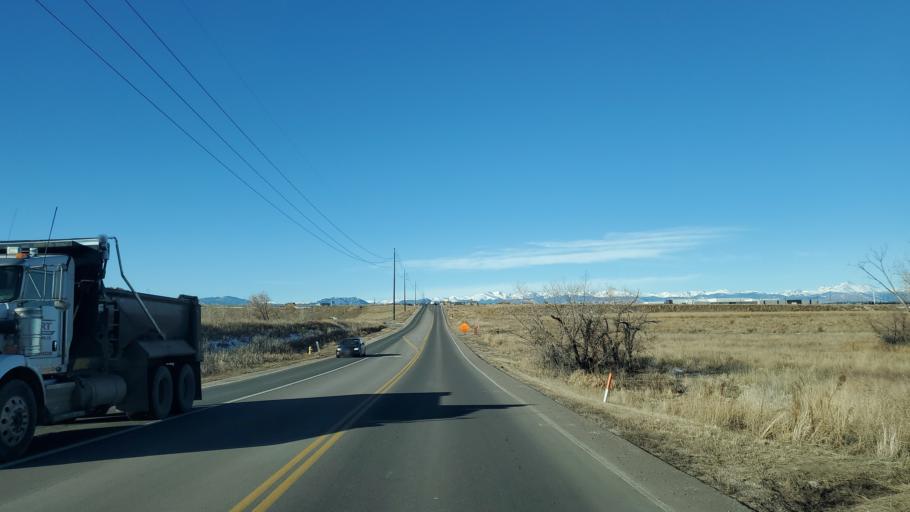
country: US
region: Colorado
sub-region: Boulder County
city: Erie
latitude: 39.9868
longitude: -105.0128
